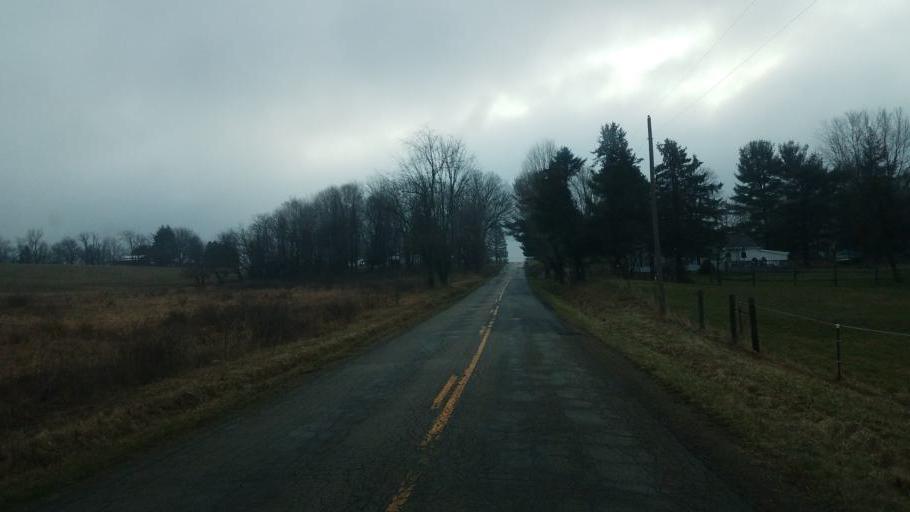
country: US
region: Ohio
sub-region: Sandusky County
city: Bellville
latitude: 40.5378
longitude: -82.4128
